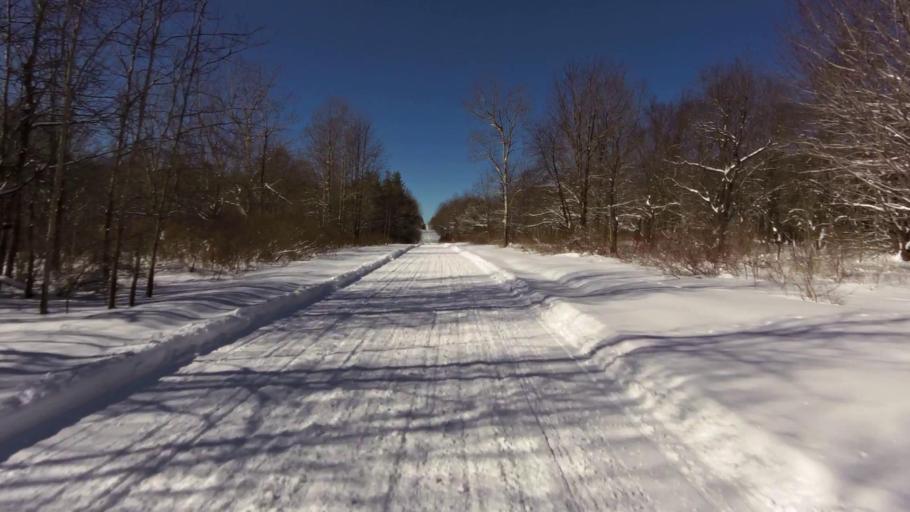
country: US
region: New York
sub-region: Chautauqua County
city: Lakewood
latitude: 42.2295
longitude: -79.3485
